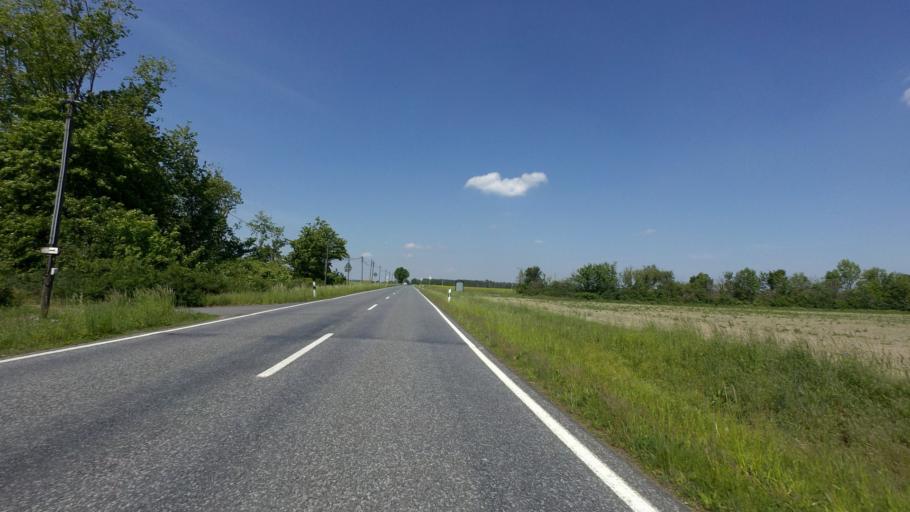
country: DE
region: Brandenburg
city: Luckau
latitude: 51.8232
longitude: 13.7929
